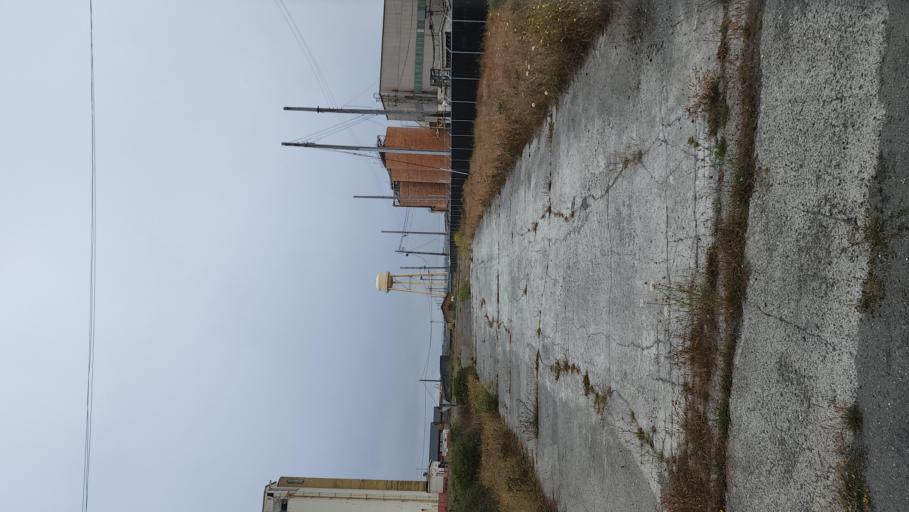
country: US
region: California
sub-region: Humboldt County
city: Eureka
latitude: 40.8064
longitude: -124.1961
